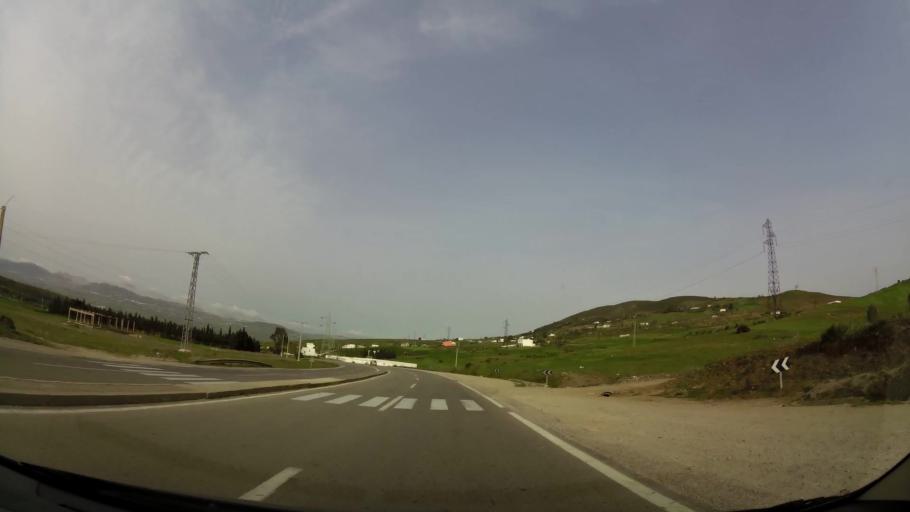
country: MA
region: Tanger-Tetouan
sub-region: Tetouan
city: Saddina
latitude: 35.5536
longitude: -5.5086
